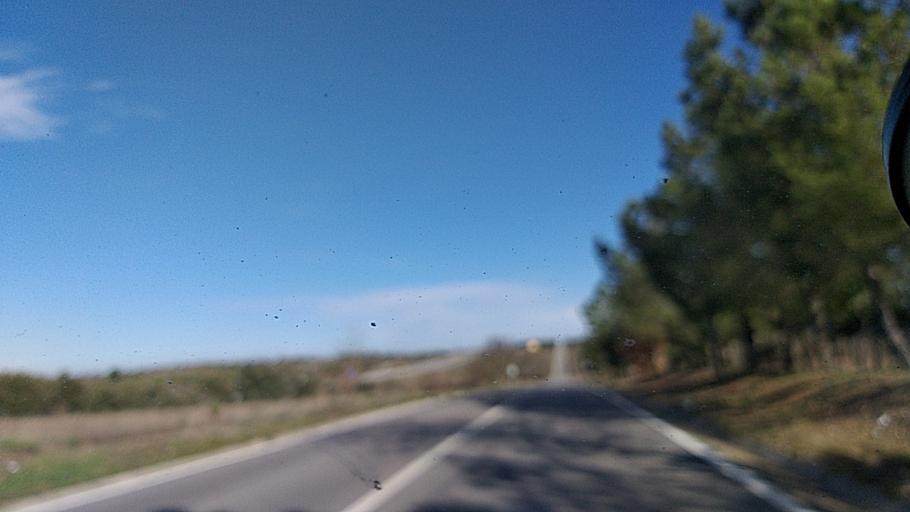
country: ES
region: Castille and Leon
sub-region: Provincia de Salamanca
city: Fuentes de Onoro
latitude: 40.6149
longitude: -6.8741
